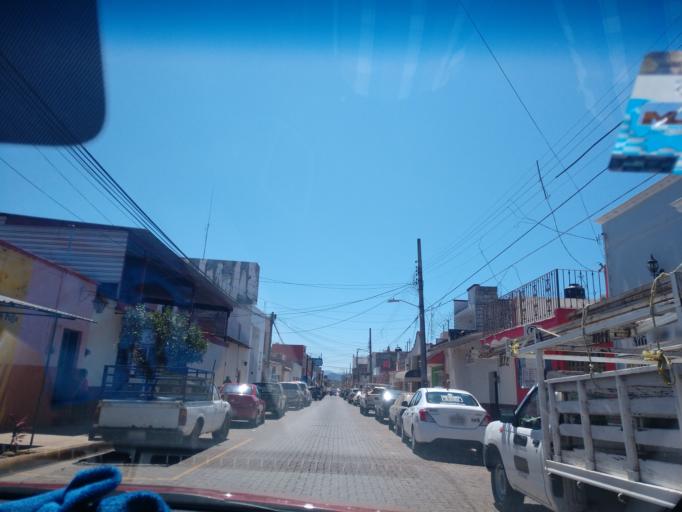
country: MX
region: Nayarit
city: Compostela
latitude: 21.2426
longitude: -104.9010
